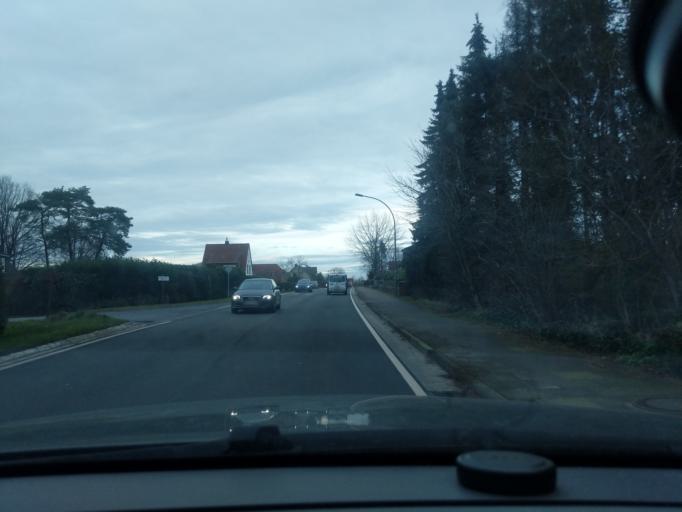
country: DE
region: Lower Saxony
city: Sauensiek
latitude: 53.3859
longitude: 9.5995
